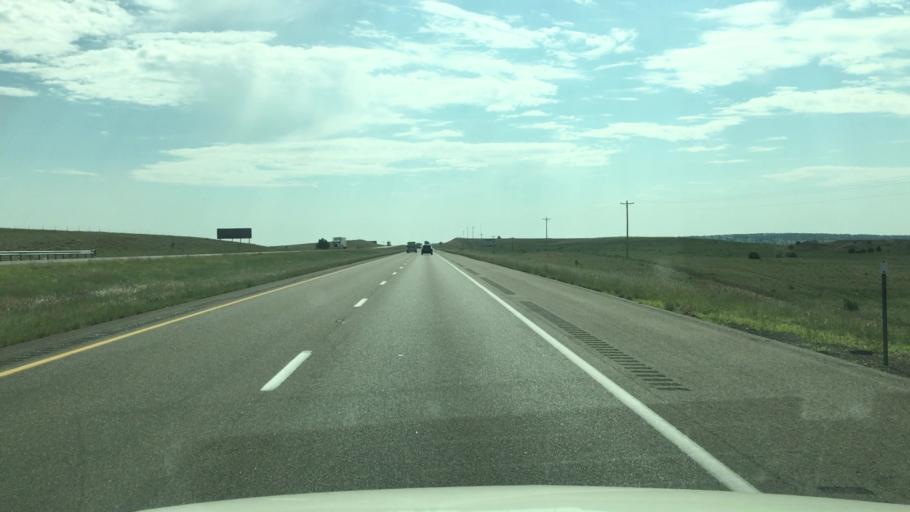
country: US
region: New Mexico
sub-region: Guadalupe County
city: Santa Rosa
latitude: 34.9902
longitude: -105.2704
